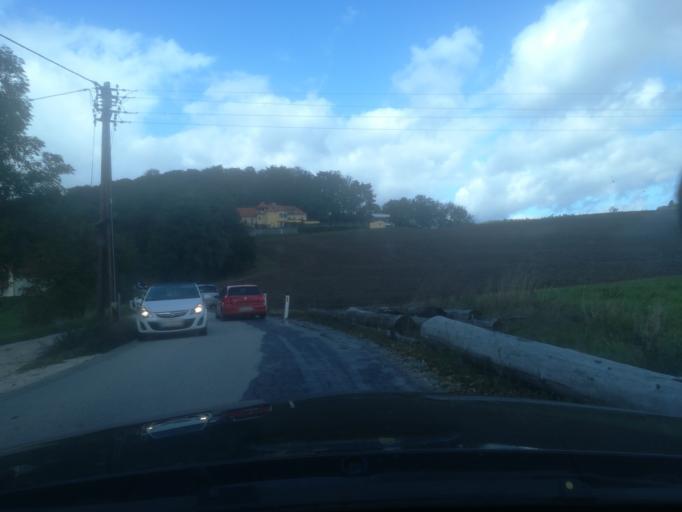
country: AT
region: Upper Austria
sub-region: Linz Stadt
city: Linz
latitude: 48.3379
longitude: 14.2741
